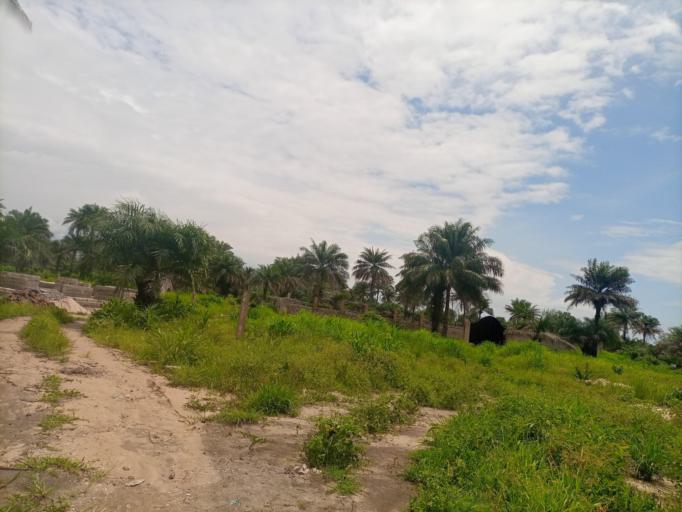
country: SL
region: Northern Province
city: Masoyila
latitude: 8.5536
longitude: -13.1688
